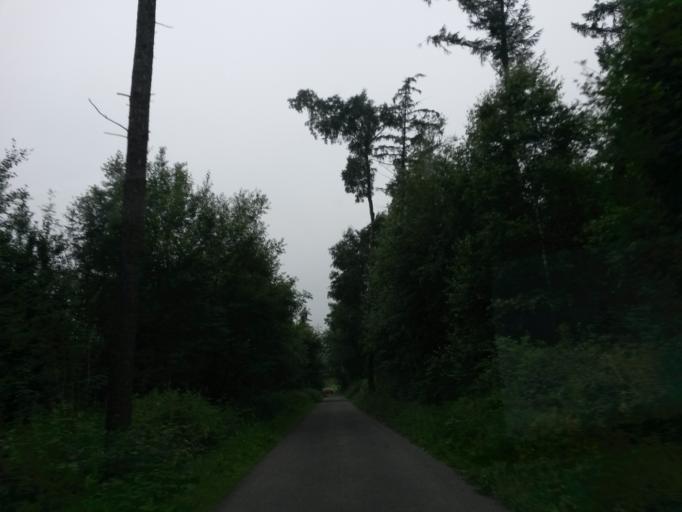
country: DE
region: North Rhine-Westphalia
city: Meinerzhagen
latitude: 51.1032
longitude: 7.6209
